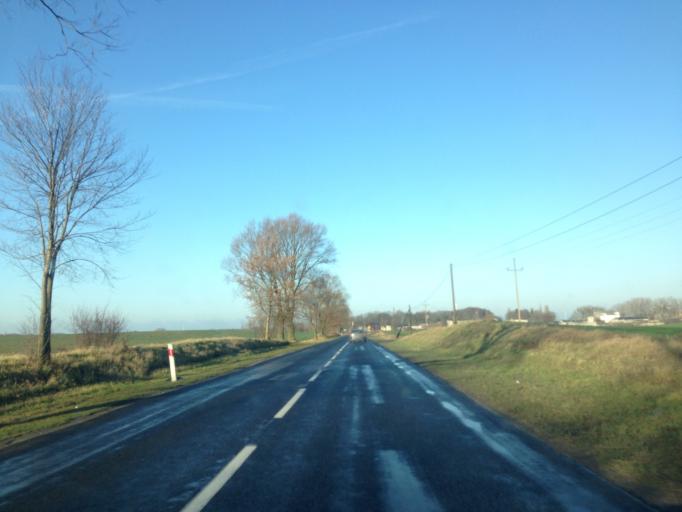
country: PL
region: Kujawsko-Pomorskie
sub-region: Powiat brodnicki
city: Bobrowo
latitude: 53.3382
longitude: 19.2224
